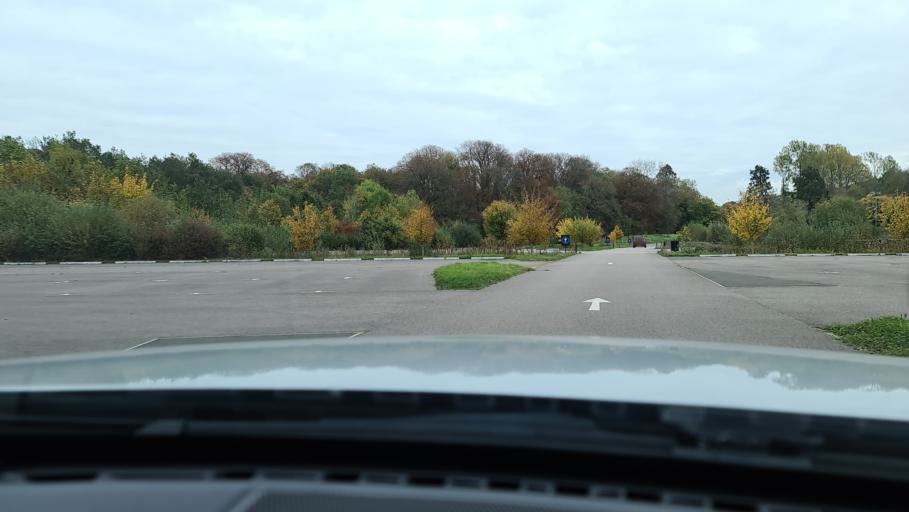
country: GB
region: England
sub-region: Buckinghamshire
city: Waddesdon
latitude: 51.8402
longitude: -0.9165
